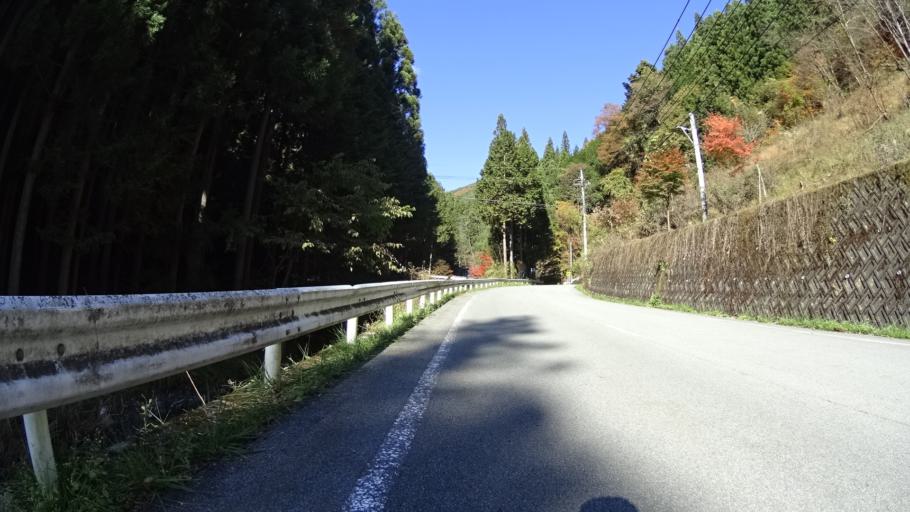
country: JP
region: Yamanashi
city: Otsuki
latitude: 35.7656
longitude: 138.9359
